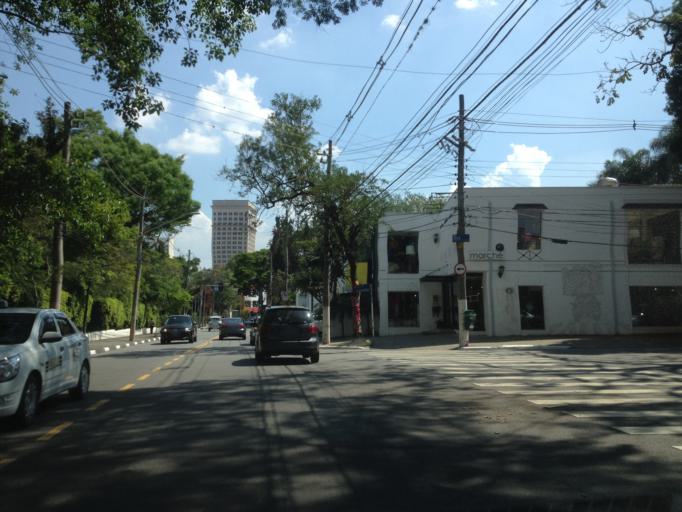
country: BR
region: Sao Paulo
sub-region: Sao Paulo
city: Sao Paulo
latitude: -23.5731
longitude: -46.6825
